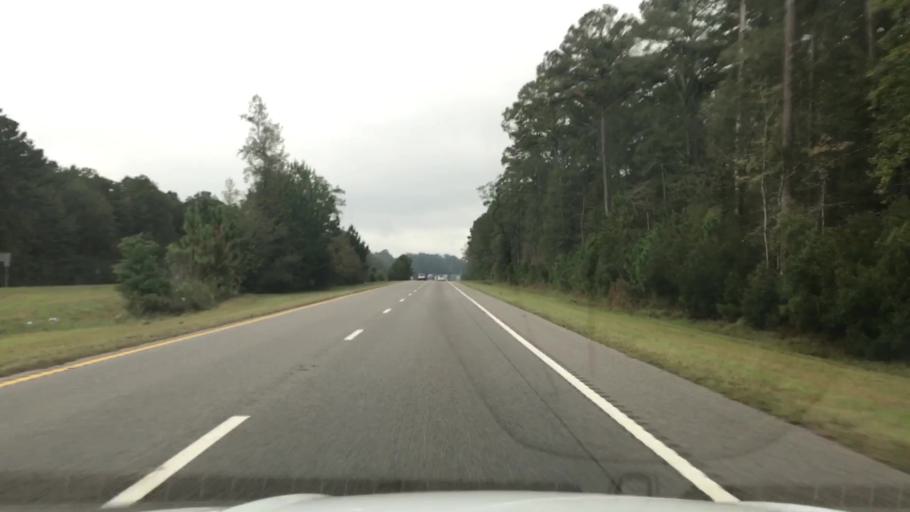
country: US
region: South Carolina
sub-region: Colleton County
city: Walterboro
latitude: 32.7376
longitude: -80.5758
